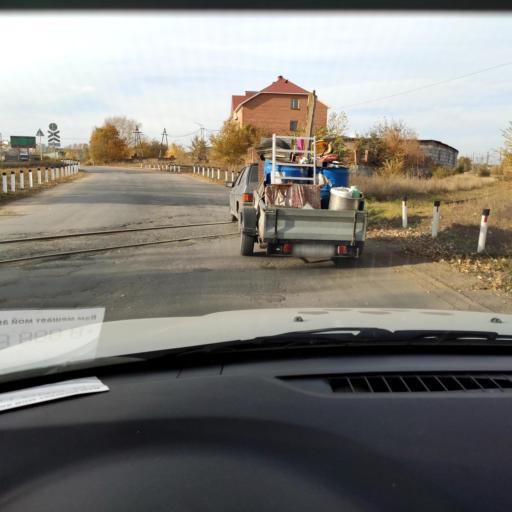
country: RU
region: Samara
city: Zhigulevsk
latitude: 53.4744
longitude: 49.5011
